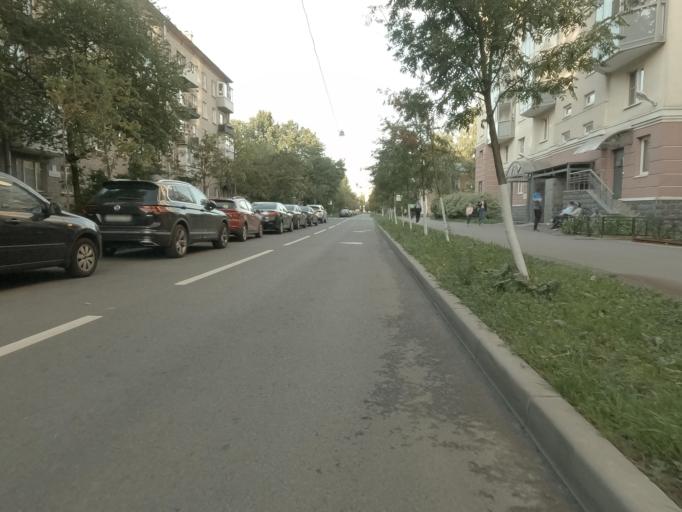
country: RU
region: St.-Petersburg
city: Admiralteisky
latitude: 59.8965
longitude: 30.2669
